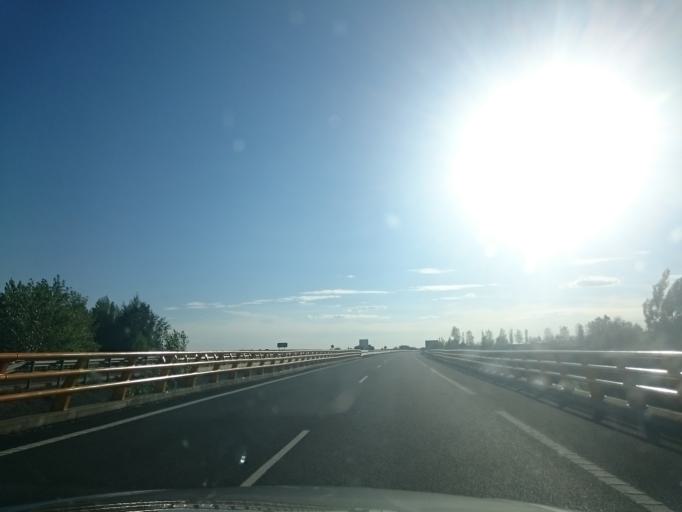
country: ES
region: Castille and Leon
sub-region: Provincia de Burgos
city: Villasandino
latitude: 42.3936
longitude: -4.0877
